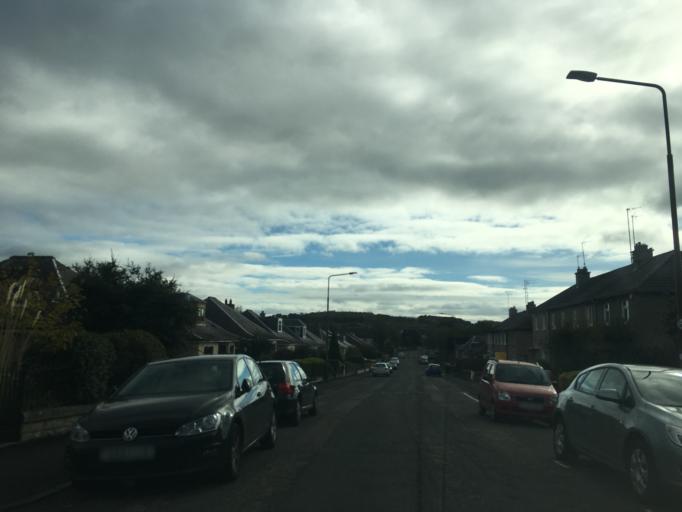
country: GB
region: Scotland
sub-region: West Lothian
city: Seafield
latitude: 55.9344
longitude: -3.1590
